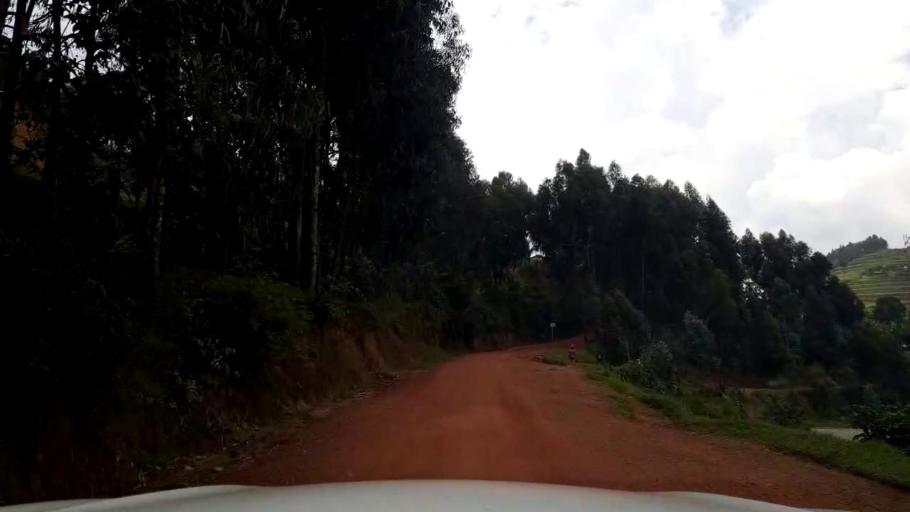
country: RW
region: Northern Province
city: Byumba
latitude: -1.5270
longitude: 29.9641
